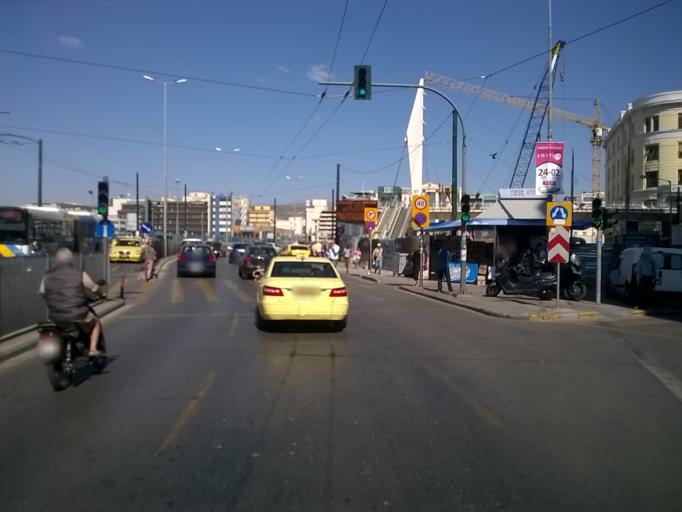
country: GR
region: Attica
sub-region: Nomos Attikis
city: Piraeus
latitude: 37.9470
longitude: 23.6423
